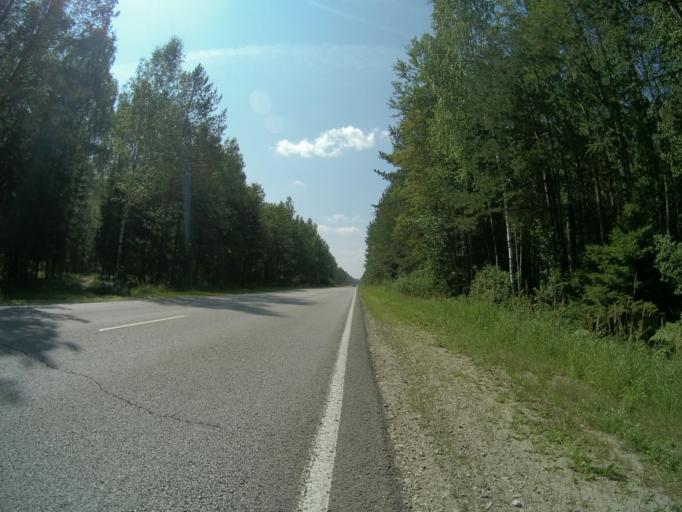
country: RU
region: Vladimir
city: Anopino
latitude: 55.6789
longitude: 40.7405
